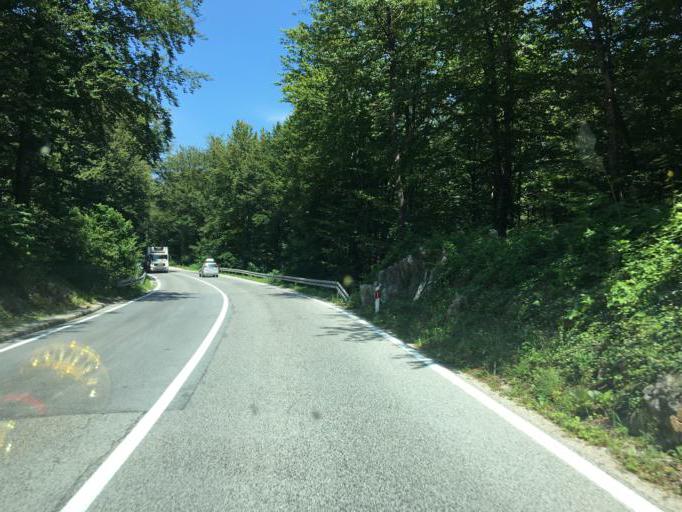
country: HR
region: Licko-Senjska
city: Jezerce
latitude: 44.8741
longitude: 15.6331
